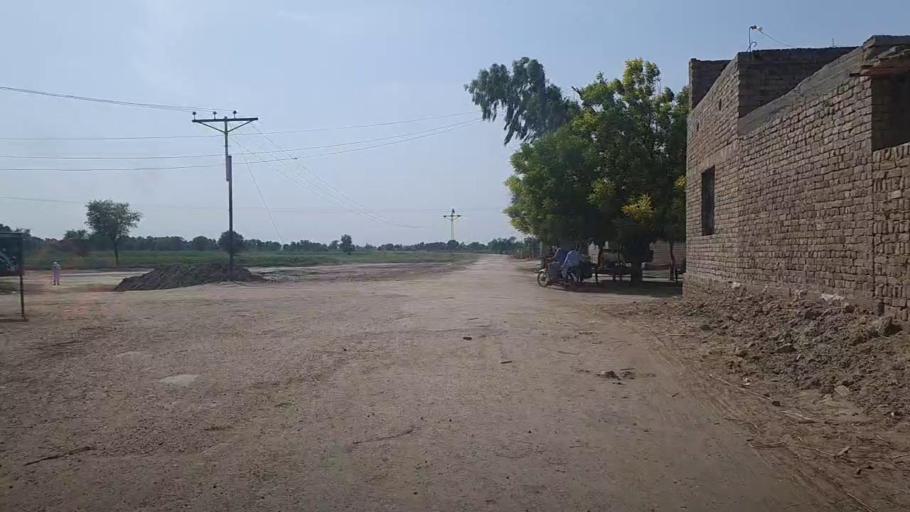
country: PK
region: Sindh
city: Ubauro
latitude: 28.1371
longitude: 69.8243
